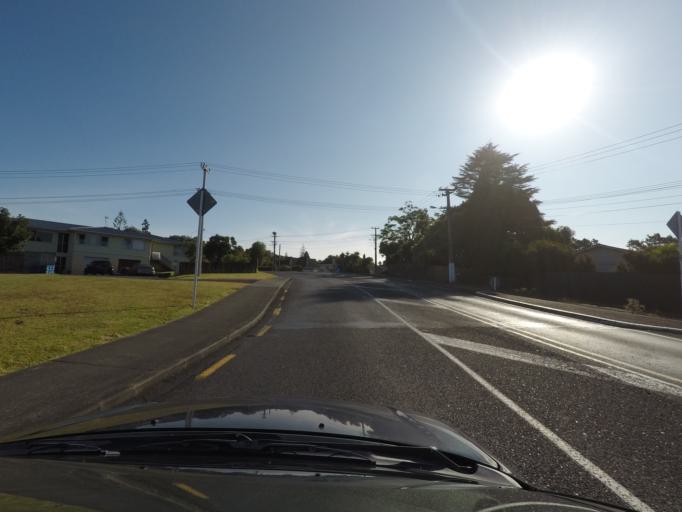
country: NZ
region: Auckland
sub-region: Auckland
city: Rosebank
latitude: -36.8688
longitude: 174.6047
